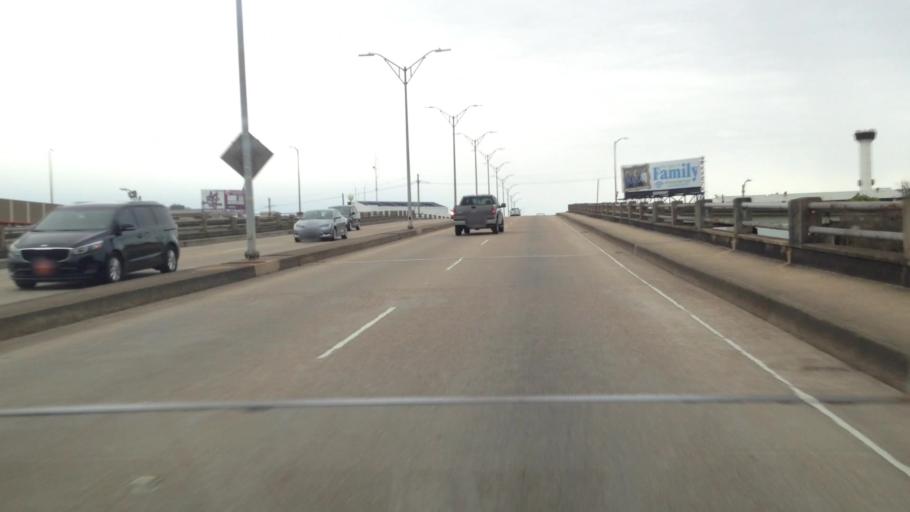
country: US
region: Louisiana
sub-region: Orleans Parish
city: New Orleans
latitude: 29.9544
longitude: -90.0966
